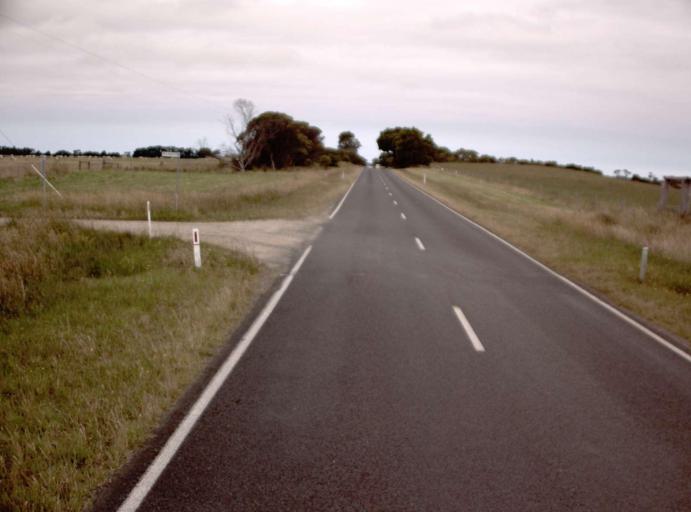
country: AU
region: Victoria
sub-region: Wellington
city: Sale
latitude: -38.5349
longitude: 146.8979
